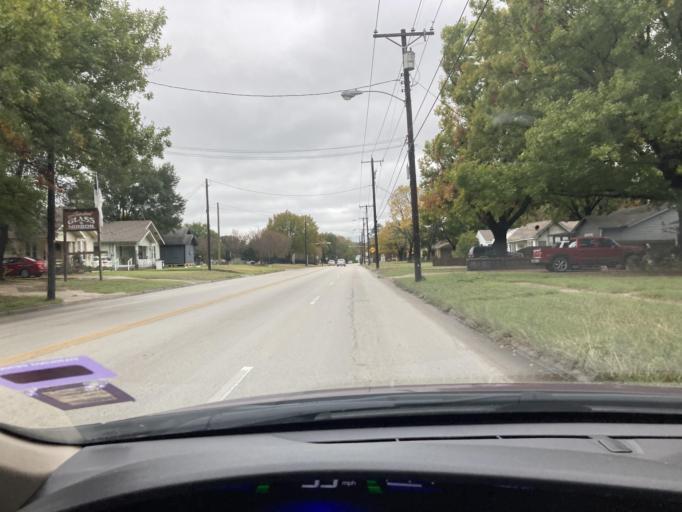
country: US
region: Texas
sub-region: Navarro County
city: Corsicana
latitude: 32.0866
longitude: -96.4879
